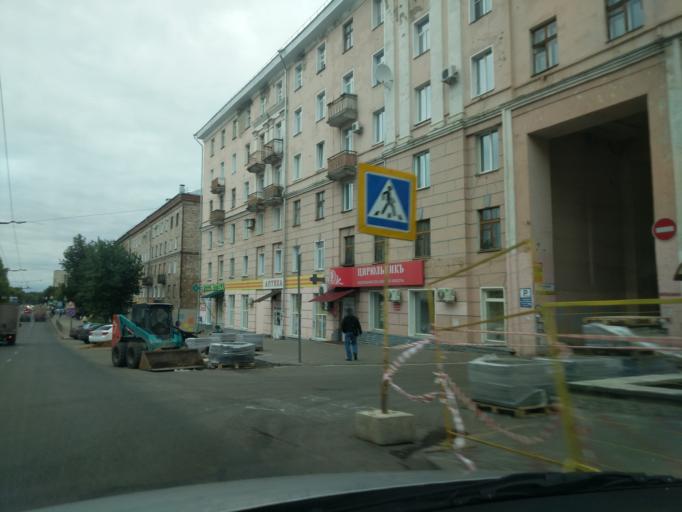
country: RU
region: Kirov
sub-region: Kirovo-Chepetskiy Rayon
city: Kirov
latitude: 58.6066
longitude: 49.6676
